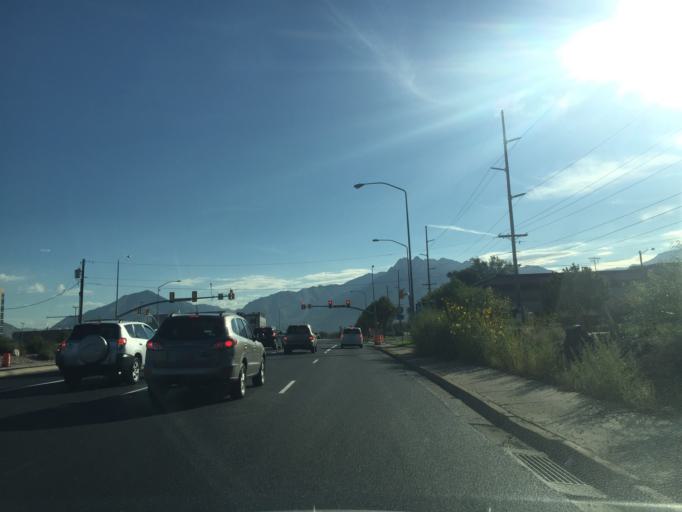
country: US
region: Utah
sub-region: Salt Lake County
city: Murray
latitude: 40.6555
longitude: -111.8953
